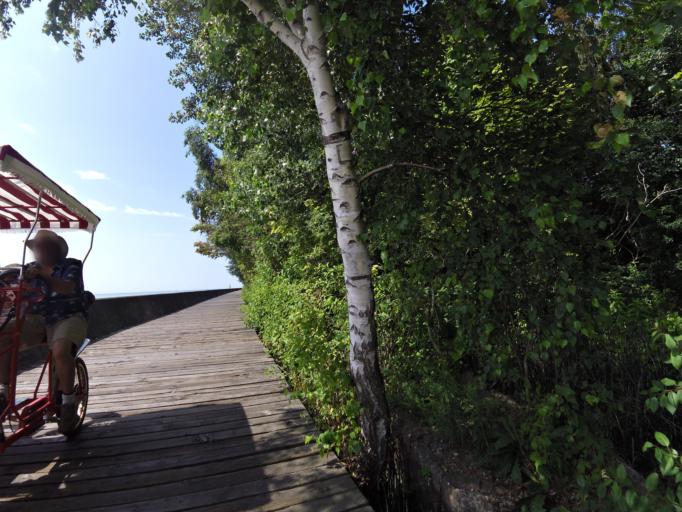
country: CA
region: Ontario
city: Toronto
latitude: 43.6256
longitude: -79.3578
